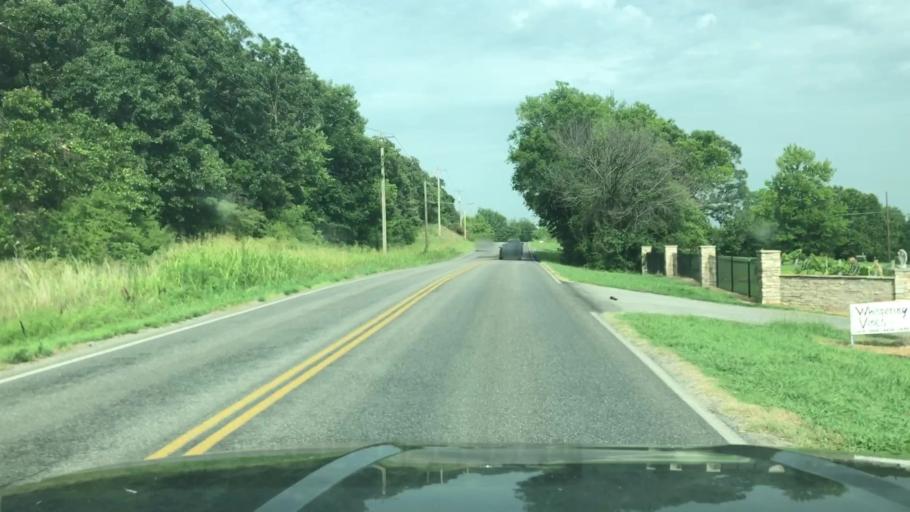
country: US
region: Oklahoma
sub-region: Tulsa County
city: Oakhurst
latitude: 36.0890
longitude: -96.0753
